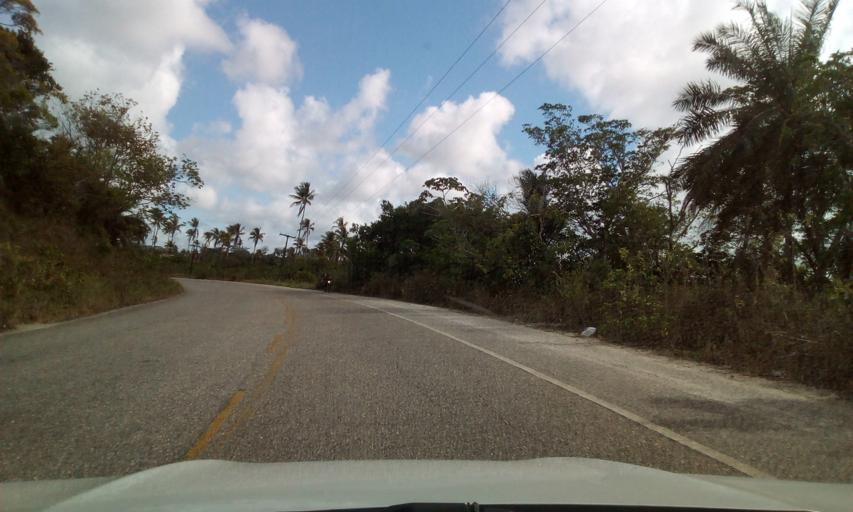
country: BR
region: Sergipe
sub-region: Estancia
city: Estancia
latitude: -11.3803
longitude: -37.4636
